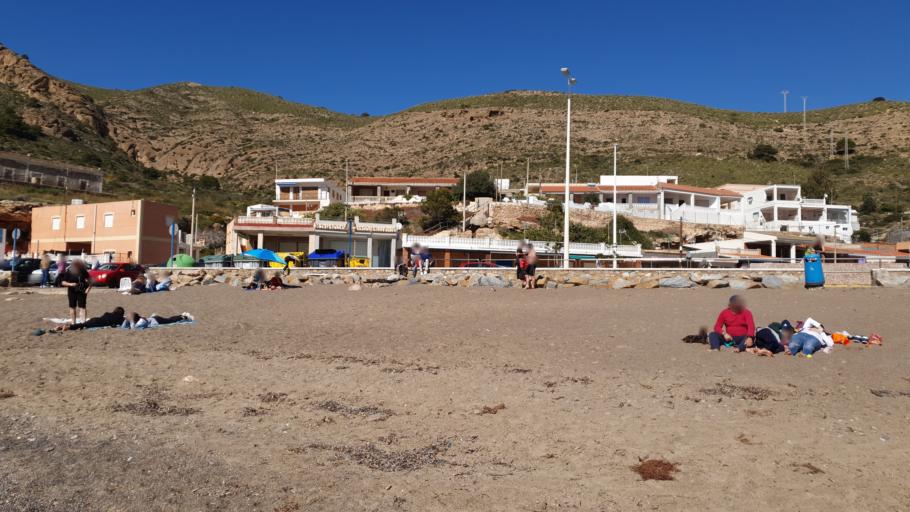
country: ES
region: Murcia
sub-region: Murcia
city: Cartagena
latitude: 37.5842
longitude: -1.0734
